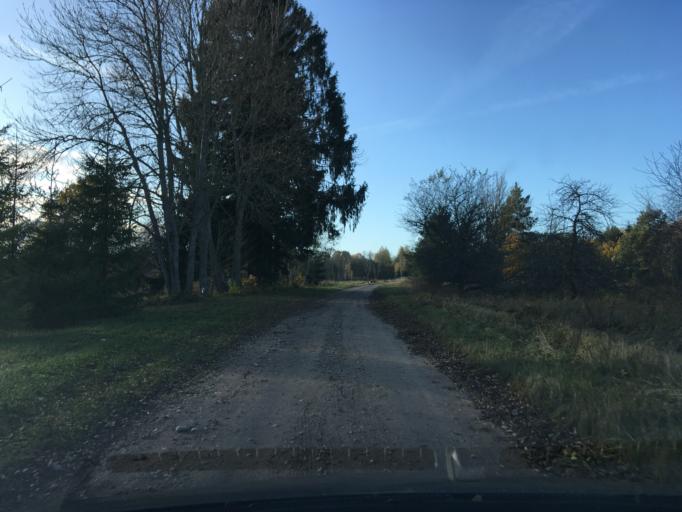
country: EE
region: Laeaene
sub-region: Lihula vald
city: Lihula
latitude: 58.5643
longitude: 23.7730
